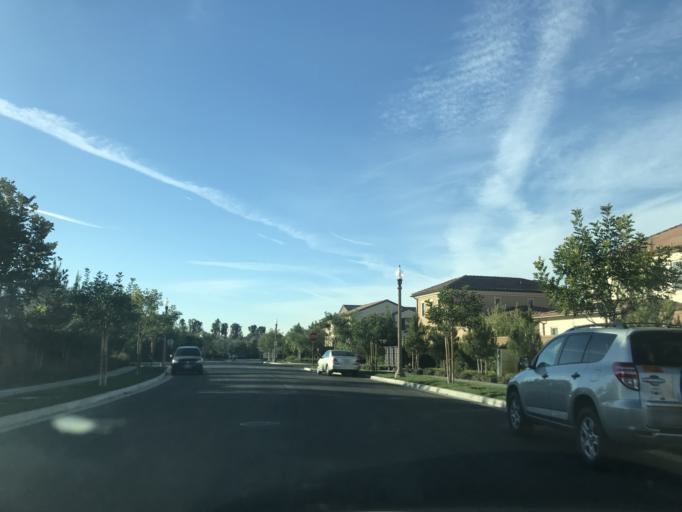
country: US
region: California
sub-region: Orange County
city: North Tustin
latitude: 33.7123
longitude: -117.7485
